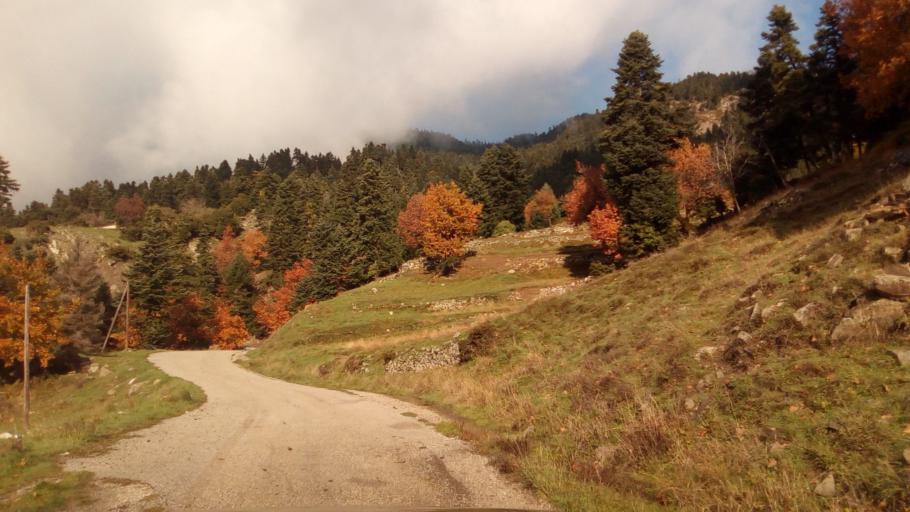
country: GR
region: West Greece
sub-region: Nomos Aitolias kai Akarnanias
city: Nafpaktos
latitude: 38.5670
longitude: 21.9240
